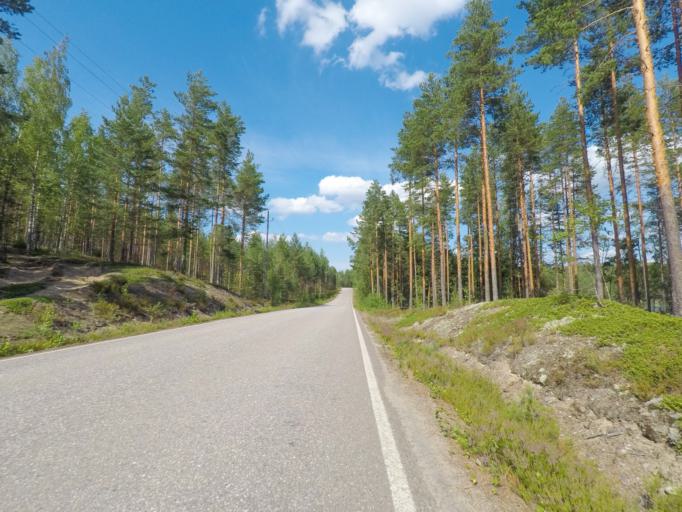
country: FI
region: Southern Savonia
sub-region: Mikkeli
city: Puumala
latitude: 61.4571
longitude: 28.1745
